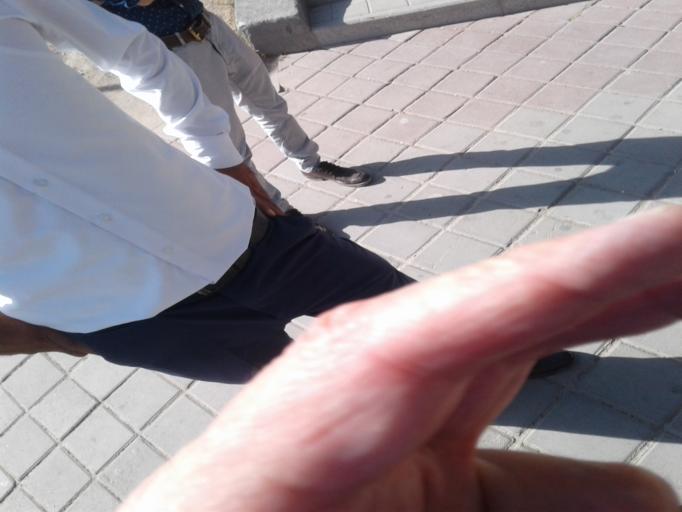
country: TJ
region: Republican Subordination
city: Hisor
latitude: 38.4836
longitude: 68.5943
